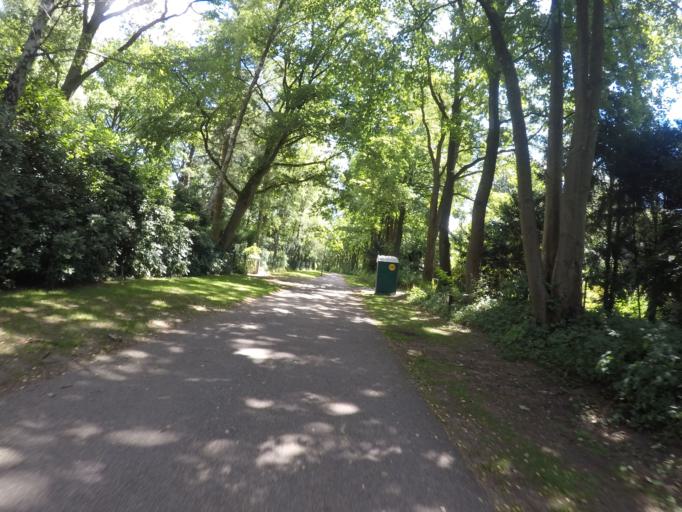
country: DE
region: Schleswig-Holstein
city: Rellingen
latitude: 53.5747
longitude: 9.7993
